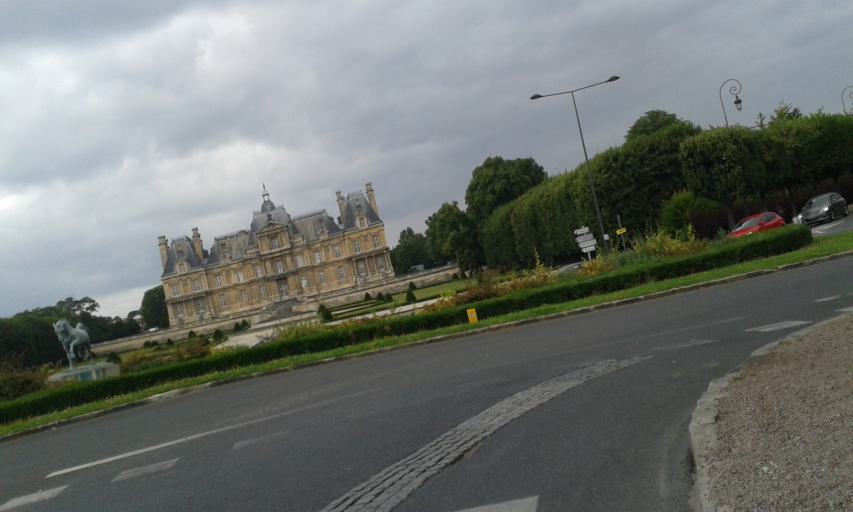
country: FR
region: Ile-de-France
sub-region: Departement des Yvelines
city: Maisons-Laffitte
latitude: 48.9457
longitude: 2.1568
